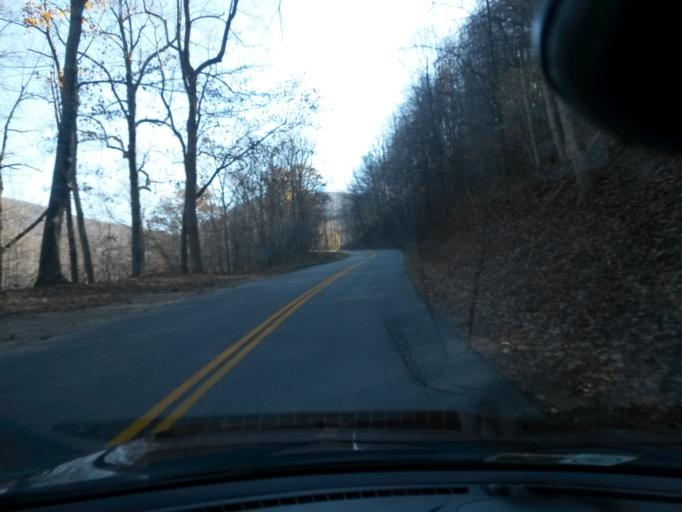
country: US
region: Virginia
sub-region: Botetourt County
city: Buchanan
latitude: 37.4717
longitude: -79.6399
